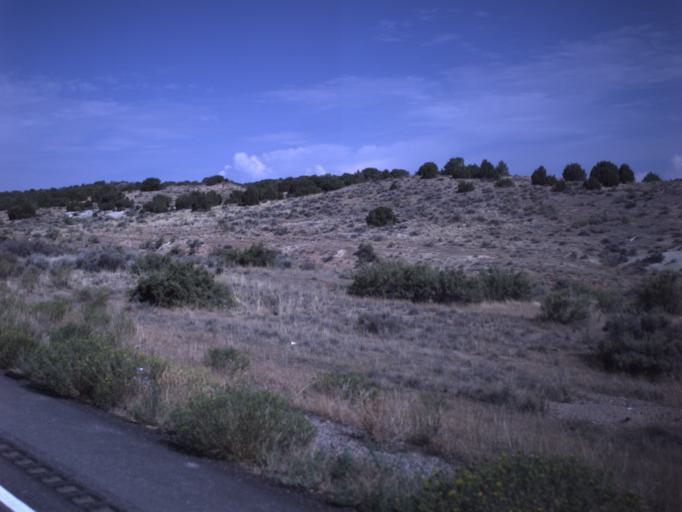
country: US
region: Utah
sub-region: Uintah County
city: Naples
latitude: 40.3192
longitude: -109.2478
